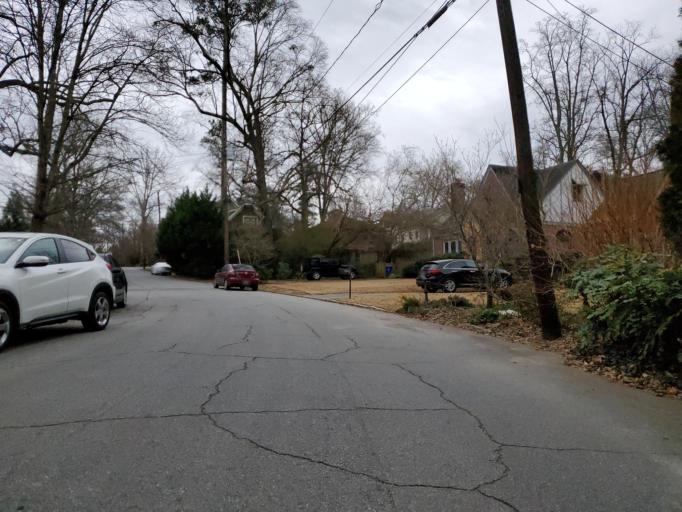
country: US
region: Georgia
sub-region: DeKalb County
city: Decatur
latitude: 33.7850
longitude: -84.2960
